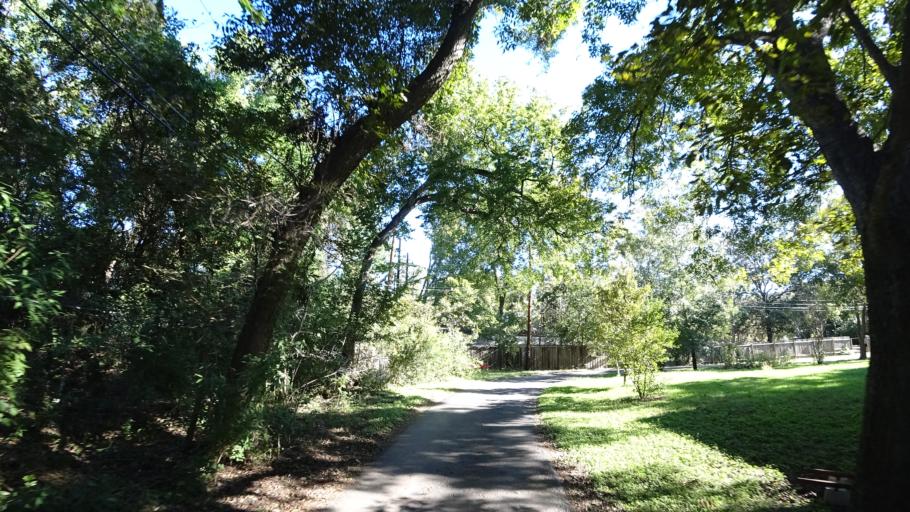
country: US
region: Texas
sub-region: Travis County
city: West Lake Hills
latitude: 30.3434
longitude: -97.7915
